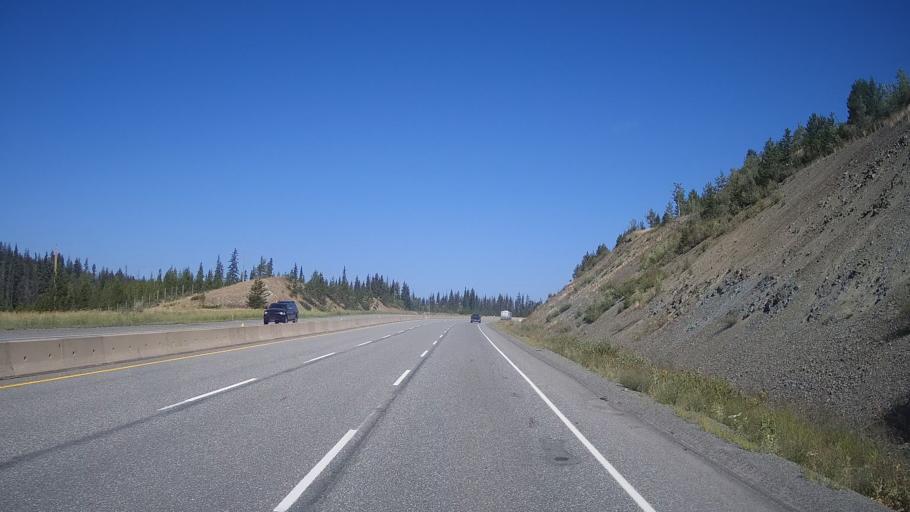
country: CA
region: British Columbia
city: Merritt
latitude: 50.3028
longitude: -120.6393
